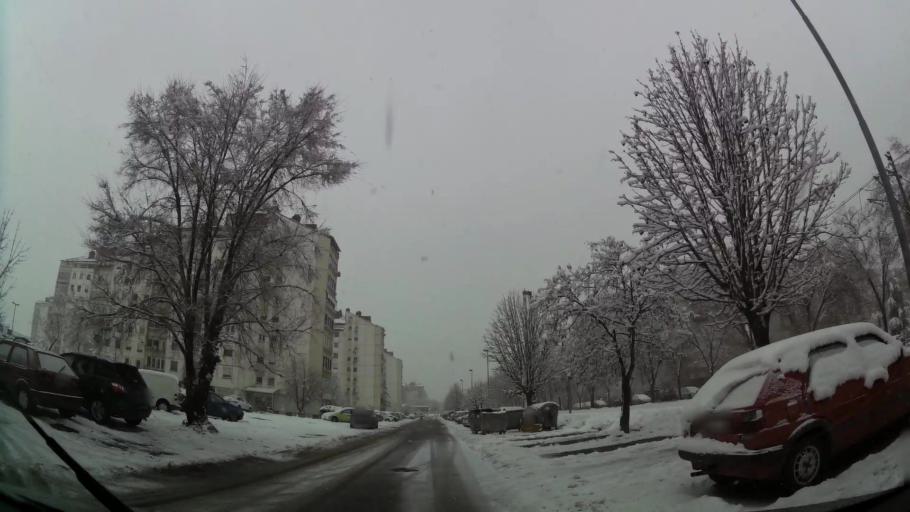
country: RS
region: Central Serbia
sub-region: Belgrade
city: Cukarica
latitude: 44.7950
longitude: 20.3730
